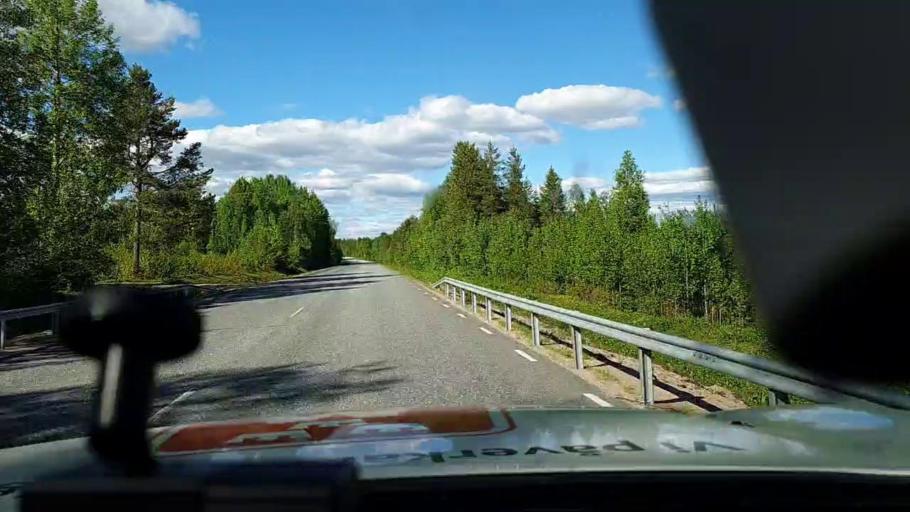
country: FI
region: Lapland
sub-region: Torniolaakso
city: Ylitornio
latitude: 66.3382
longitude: 23.6446
